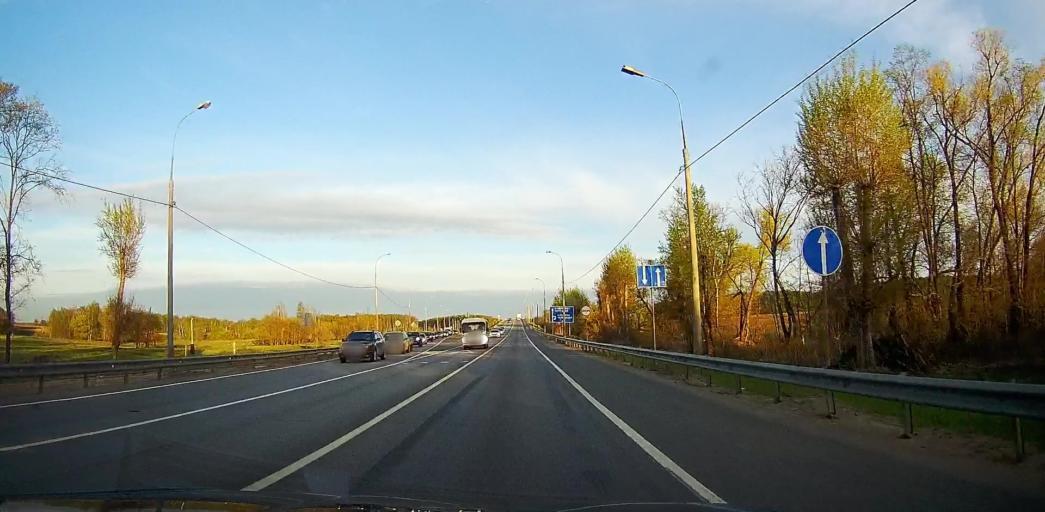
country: RU
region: Moskovskaya
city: Troitskoye
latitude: 55.2401
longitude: 38.5400
